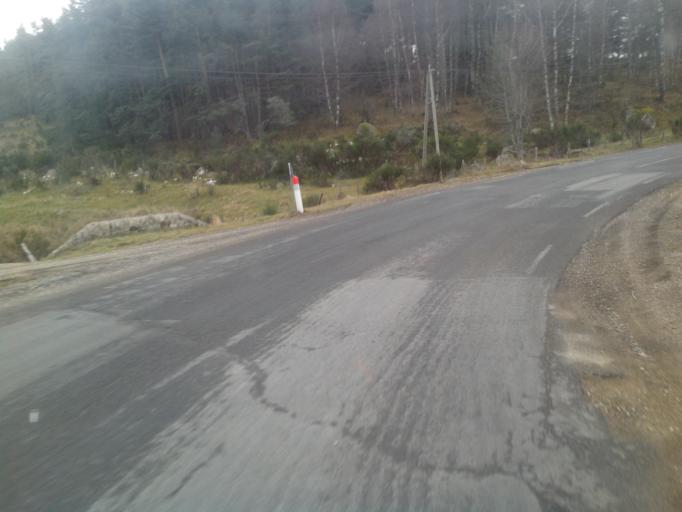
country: FR
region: Languedoc-Roussillon
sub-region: Departement de la Lozere
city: Mende
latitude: 44.6205
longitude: 3.4750
